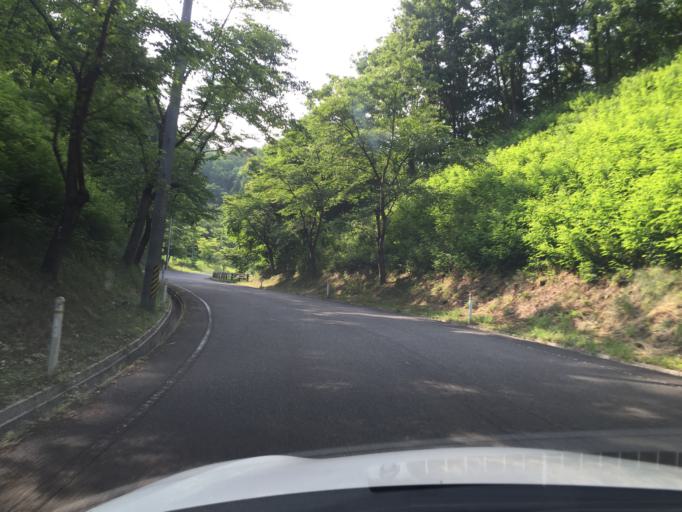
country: JP
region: Fukushima
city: Miharu
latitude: 37.3986
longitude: 140.4802
